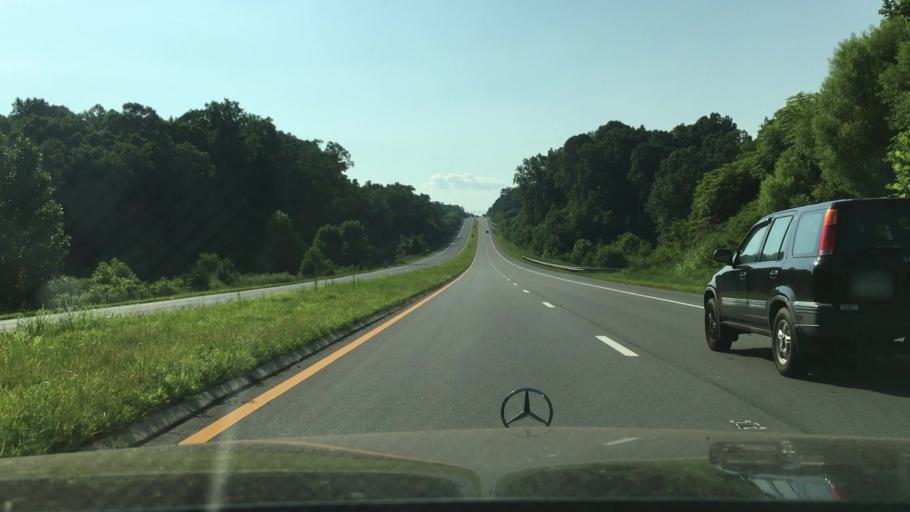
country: US
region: Virginia
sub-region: Amherst County
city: Madison Heights
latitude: 37.4155
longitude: -79.1105
